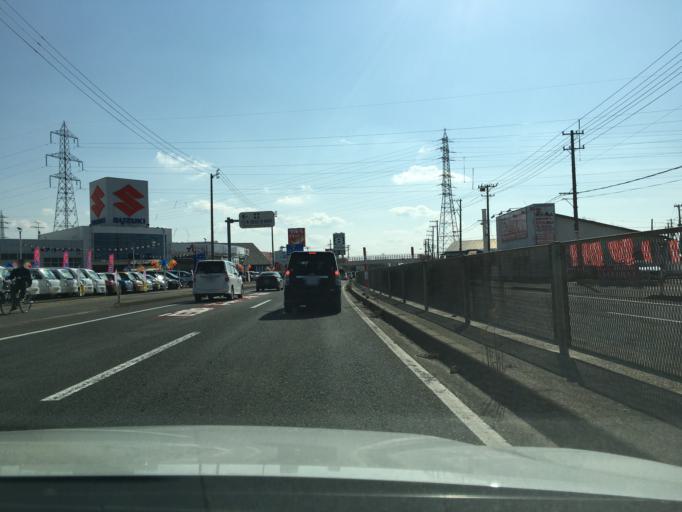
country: JP
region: Yamagata
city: Sakata
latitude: 38.8968
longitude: 139.8552
